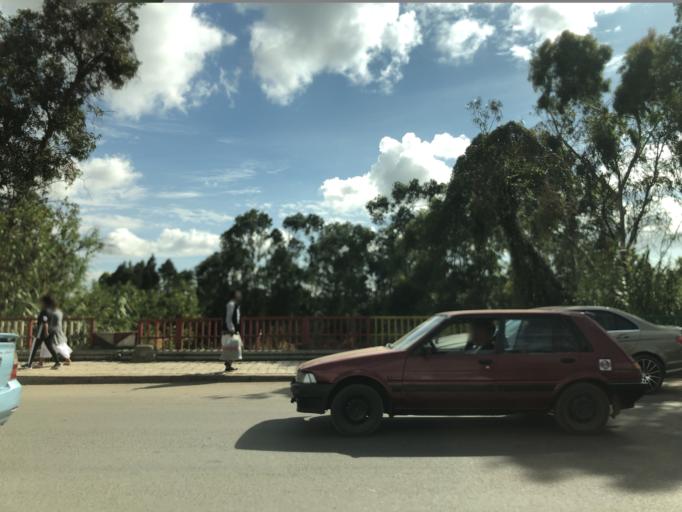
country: ET
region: Adis Abeba
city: Addis Ababa
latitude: 9.0233
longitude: 38.7798
